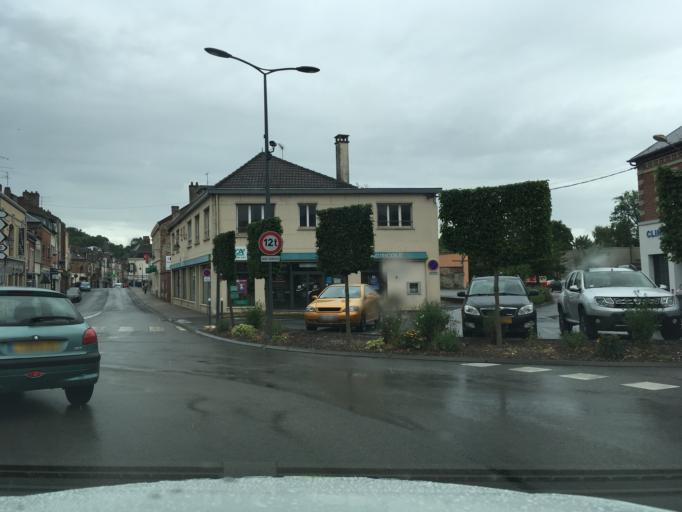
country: FR
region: Picardie
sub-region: Departement de l'Aisne
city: Guise
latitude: 49.9006
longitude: 3.6306
